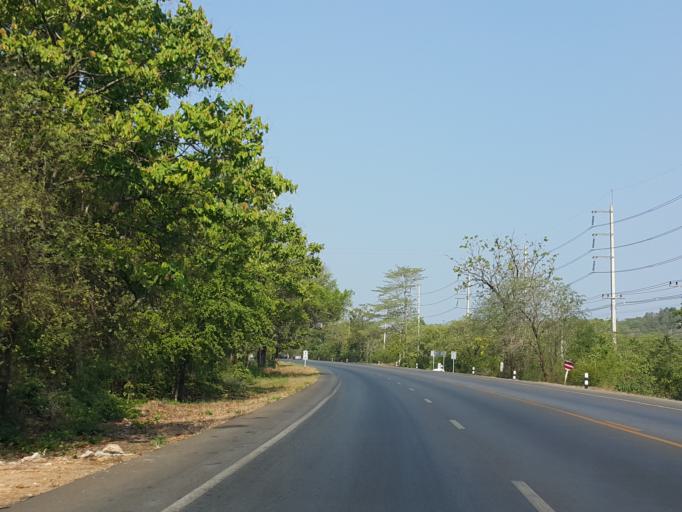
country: TH
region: Kanchanaburi
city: Sai Yok
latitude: 14.1135
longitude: 99.2039
